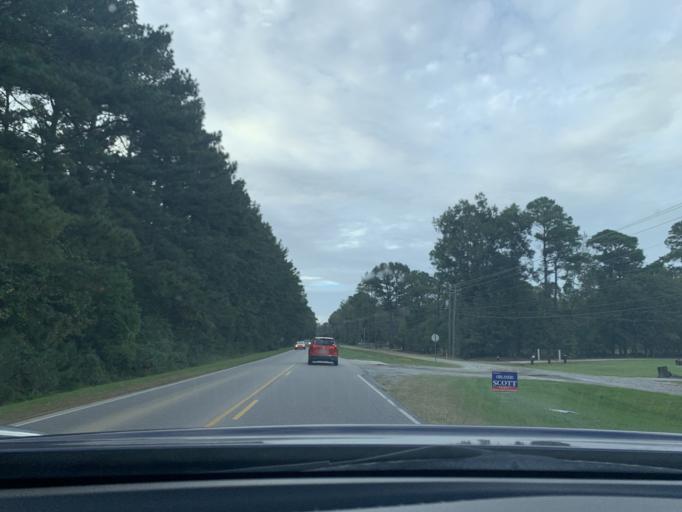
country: US
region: Georgia
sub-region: Chatham County
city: Georgetown
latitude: 32.0449
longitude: -81.2630
